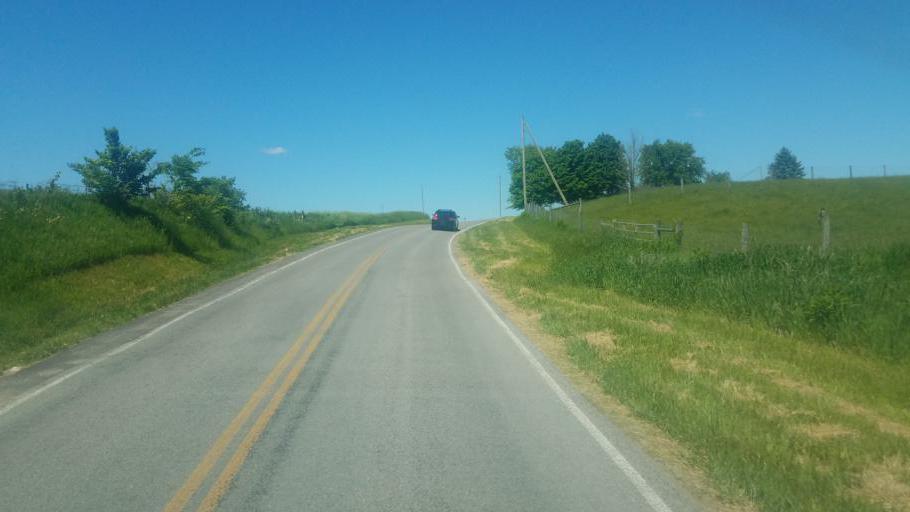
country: US
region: Ohio
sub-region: Champaign County
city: Saint Paris
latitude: 40.1904
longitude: -83.9551
